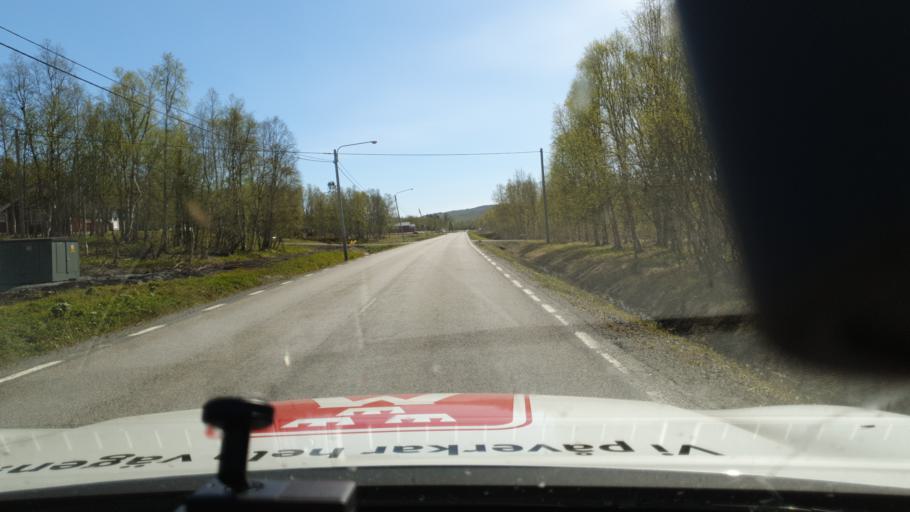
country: NO
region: Nordland
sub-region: Hattfjelldal
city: Hattfjelldal
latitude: 65.7441
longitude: 15.0094
